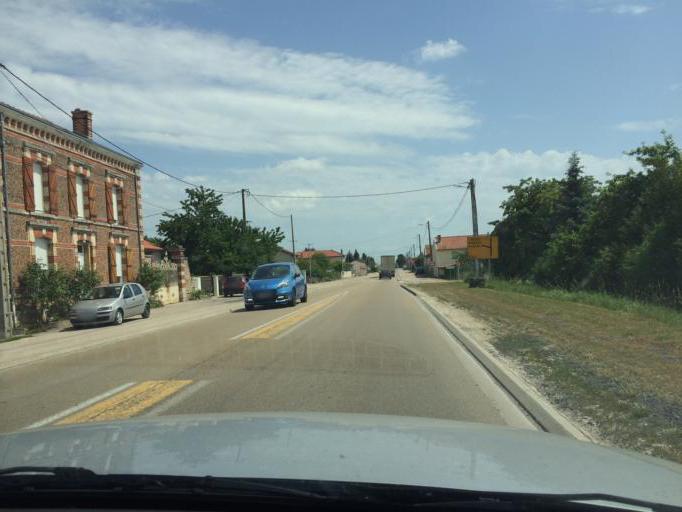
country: FR
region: Champagne-Ardenne
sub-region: Departement de la Marne
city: Sarry
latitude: 48.9011
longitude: 4.4410
